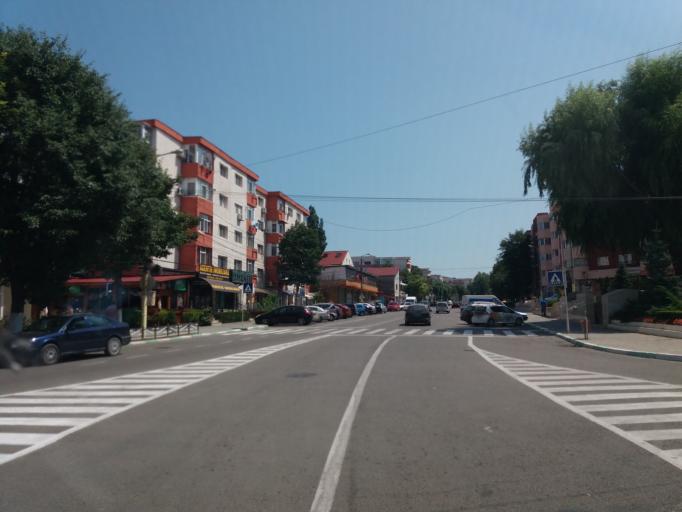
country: RO
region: Constanta
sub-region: Comuna Navodari
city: Navodari
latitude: 44.3211
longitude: 28.6082
